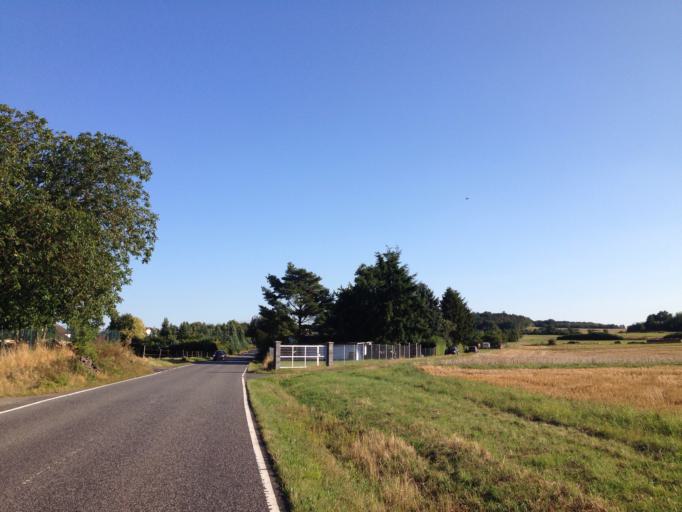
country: DE
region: Hesse
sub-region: Regierungsbezirk Giessen
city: Lich
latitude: 50.5361
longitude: 8.7460
